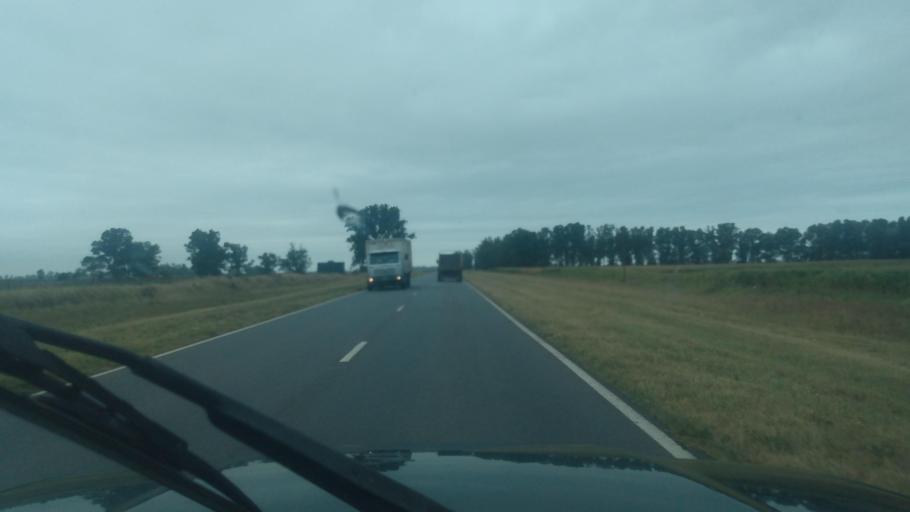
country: AR
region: Buenos Aires
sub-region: Partido de Nueve de Julio
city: Nueve de Julio
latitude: -35.4062
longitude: -60.7713
